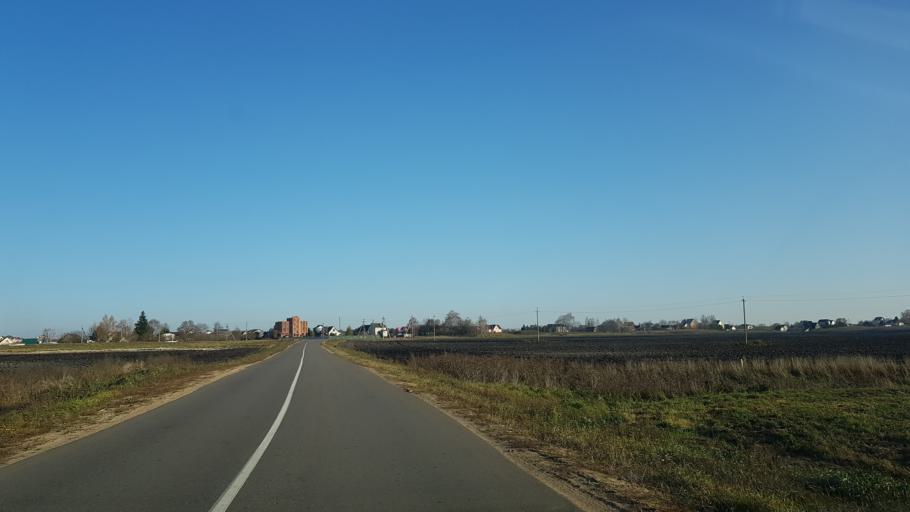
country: BY
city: Fanipol
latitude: 53.7202
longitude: 27.3063
